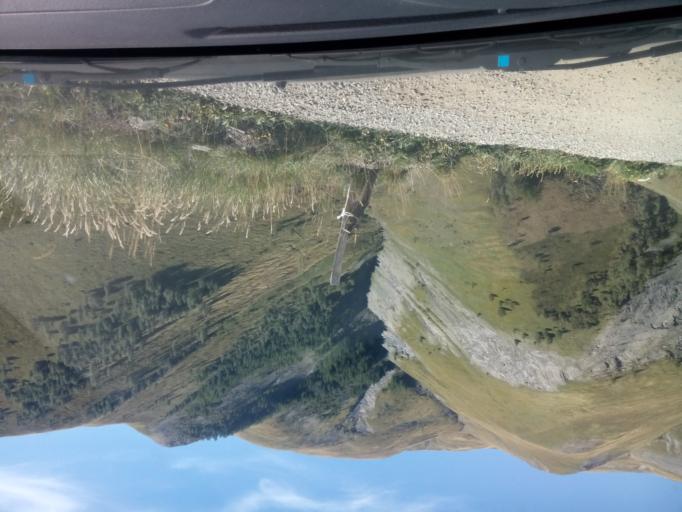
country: FR
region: Rhone-Alpes
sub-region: Departement de l'Isere
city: Mont-de-Lans
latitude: 45.0726
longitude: 6.1825
